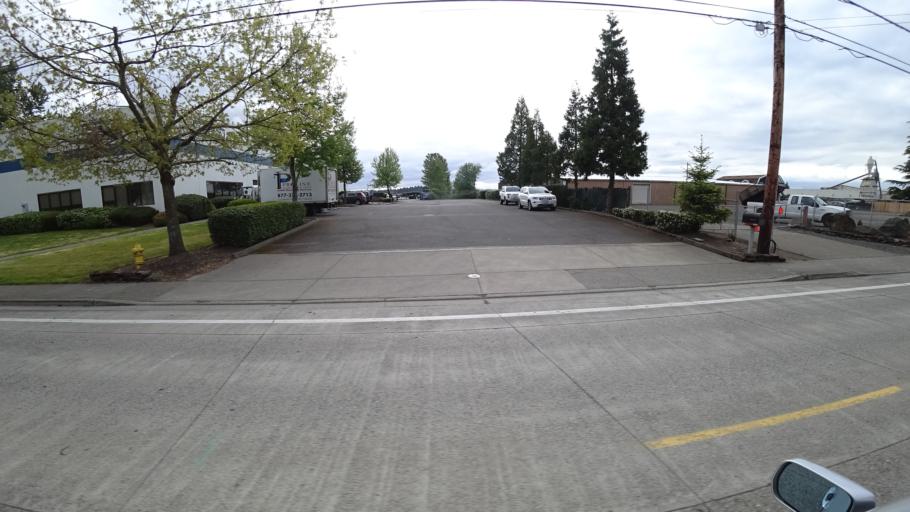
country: US
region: Oregon
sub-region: Washington County
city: Hillsboro
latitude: 45.5362
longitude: -122.9571
